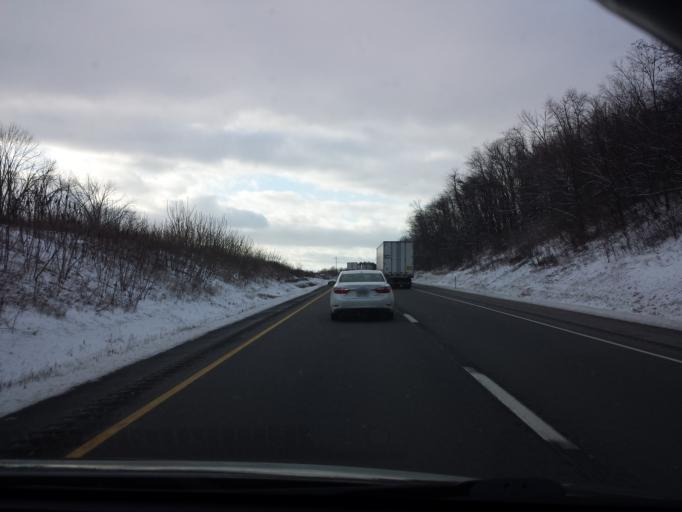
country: US
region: Pennsylvania
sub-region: Columbia County
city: Mifflinville
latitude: 41.0373
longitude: -76.3469
